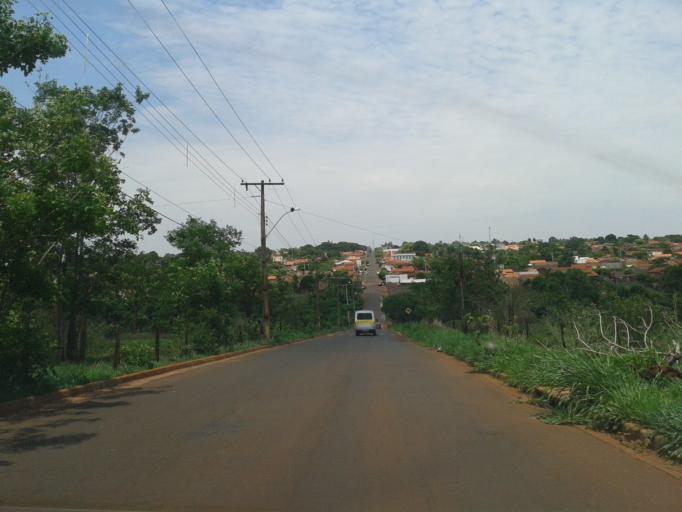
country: BR
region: Minas Gerais
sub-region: Ituiutaba
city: Ituiutaba
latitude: -18.9909
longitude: -49.4396
